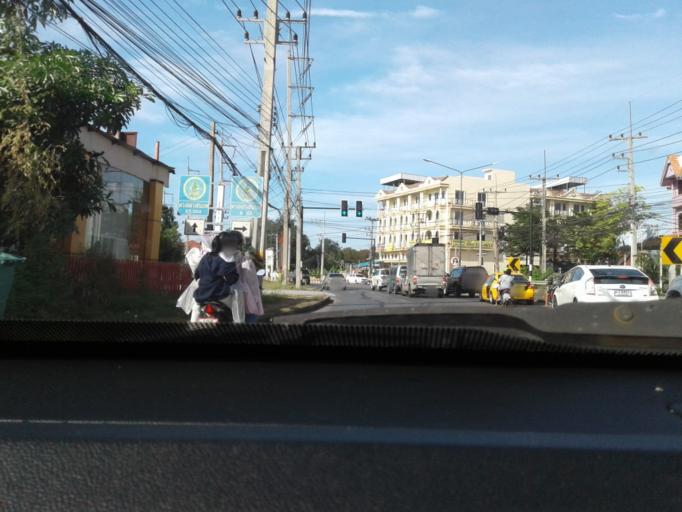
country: TH
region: Nakhon Pathom
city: Salaya
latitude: 13.8123
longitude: 100.3226
